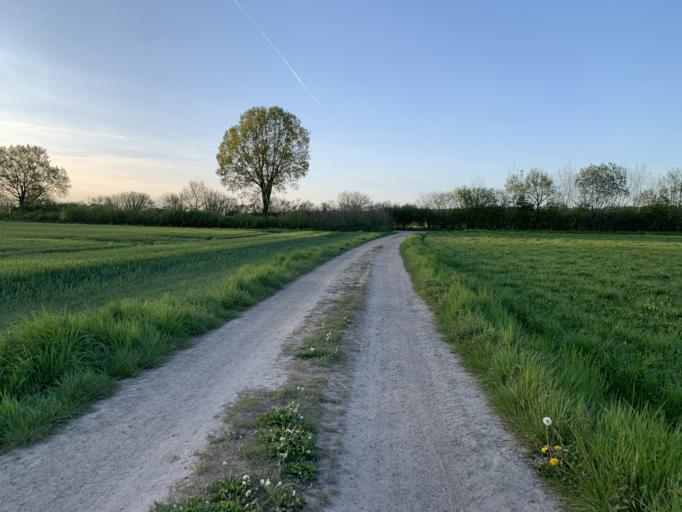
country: DE
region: Schleswig-Holstein
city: Worth
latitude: 53.4676
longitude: 10.4214
